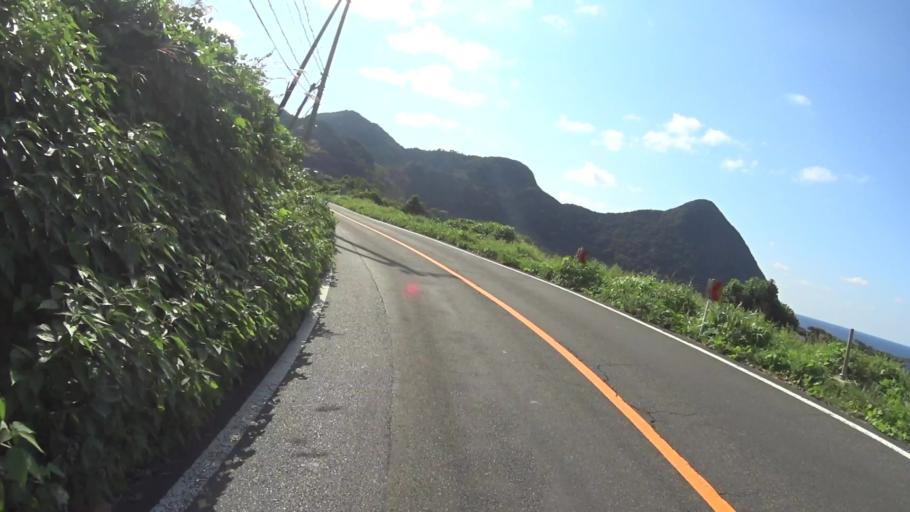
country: JP
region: Kyoto
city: Miyazu
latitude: 35.7507
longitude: 135.1522
